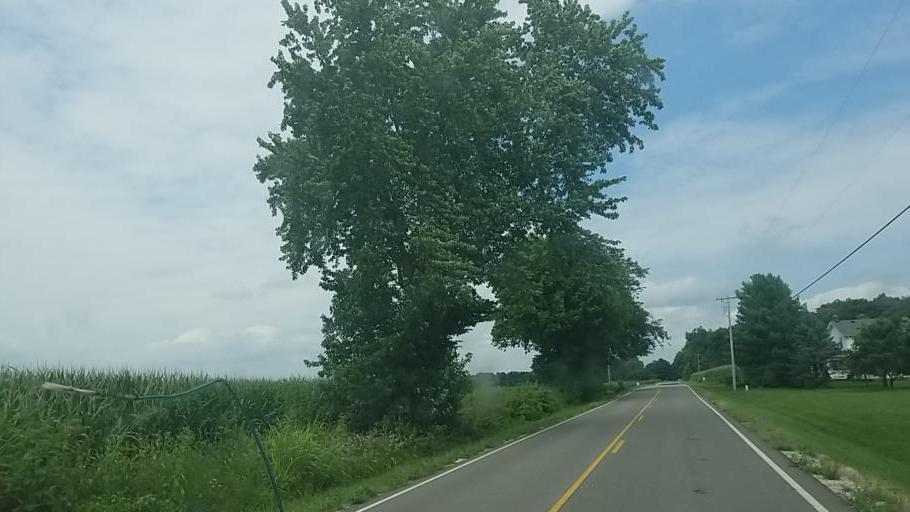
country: US
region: Ohio
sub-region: Pickaway County
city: Ashville
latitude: 39.7728
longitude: -82.9109
